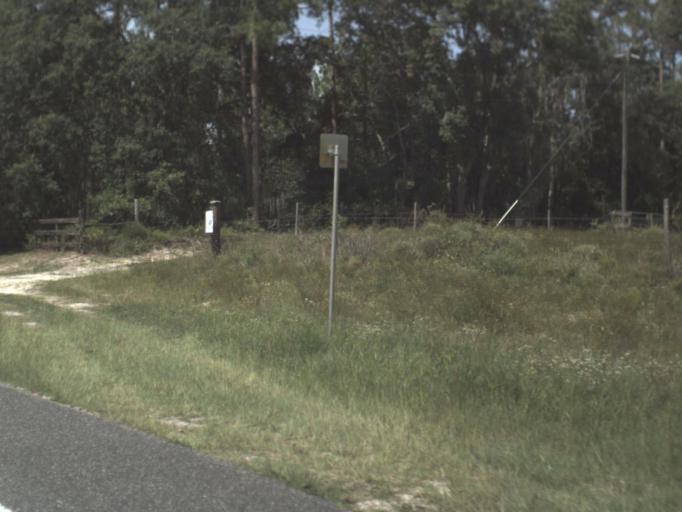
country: US
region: Florida
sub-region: Gilchrist County
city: Trenton
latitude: 29.7531
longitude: -82.7406
